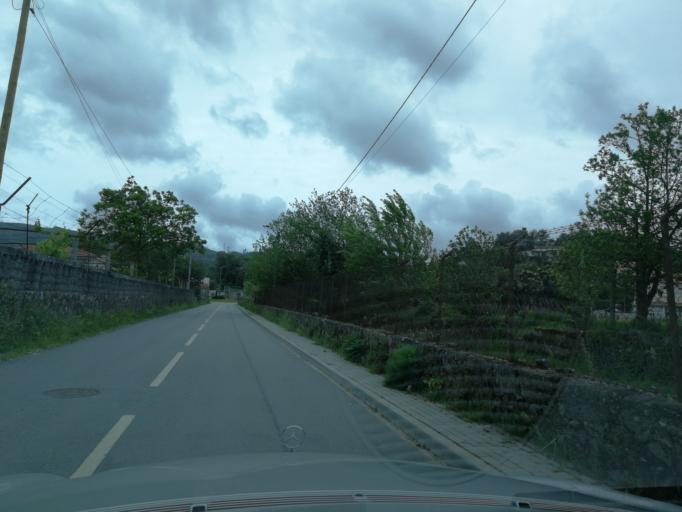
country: PT
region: Braga
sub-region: Braga
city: Adaufe
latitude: 41.5977
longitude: -8.3770
